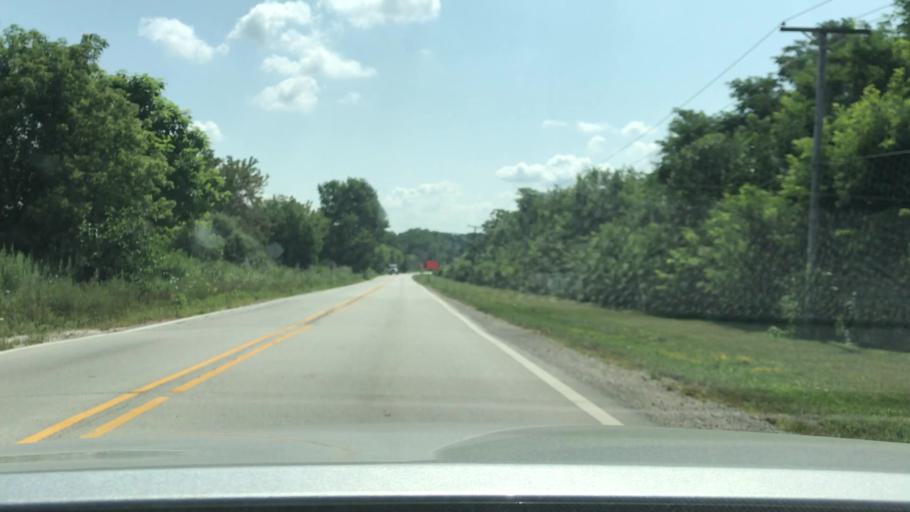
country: US
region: Illinois
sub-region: Will County
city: Bolingbrook
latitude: 41.7198
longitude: -88.0775
